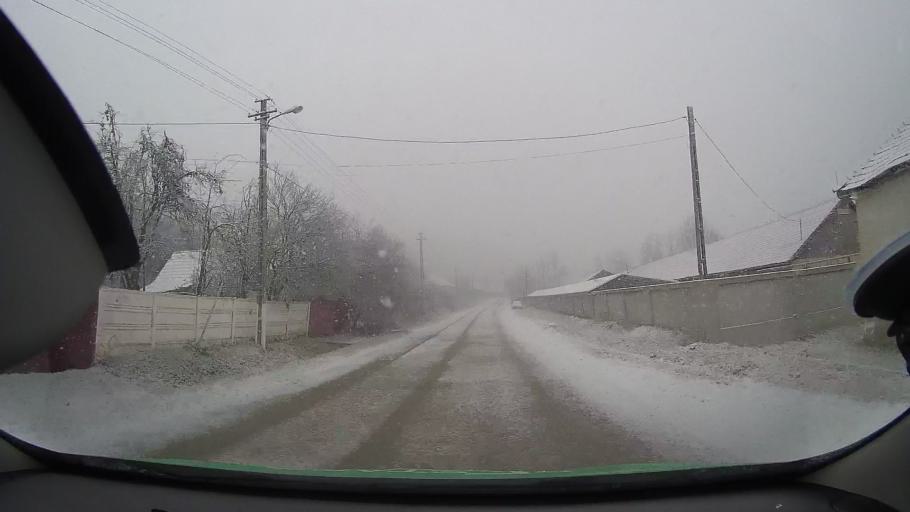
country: RO
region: Alba
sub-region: Comuna Hoparta
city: Hoparta
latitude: 46.3150
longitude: 23.8609
